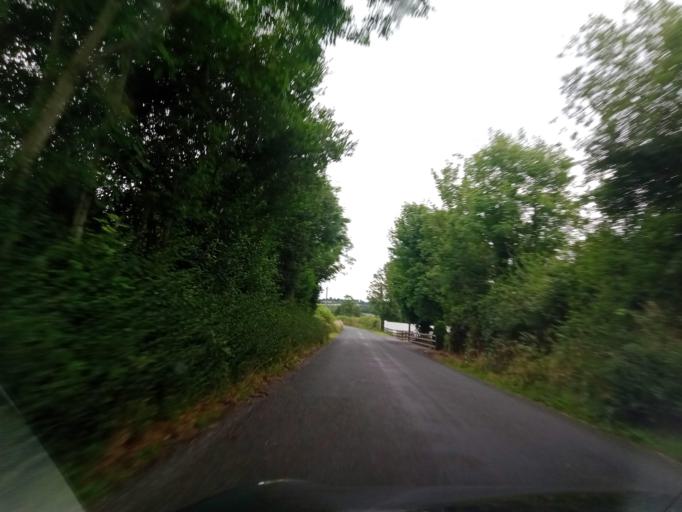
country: IE
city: Ballylinan
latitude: 52.9068
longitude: -7.0985
